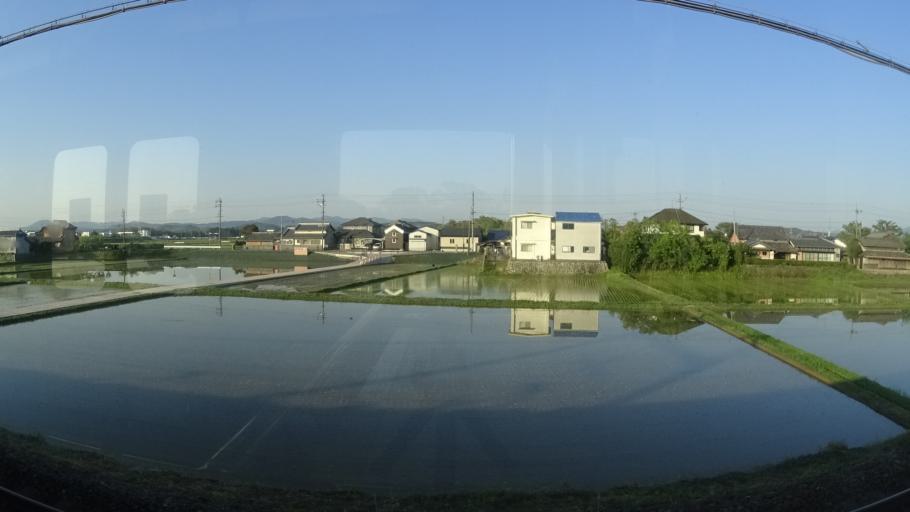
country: JP
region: Mie
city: Ise
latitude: 34.5401
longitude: 136.6031
